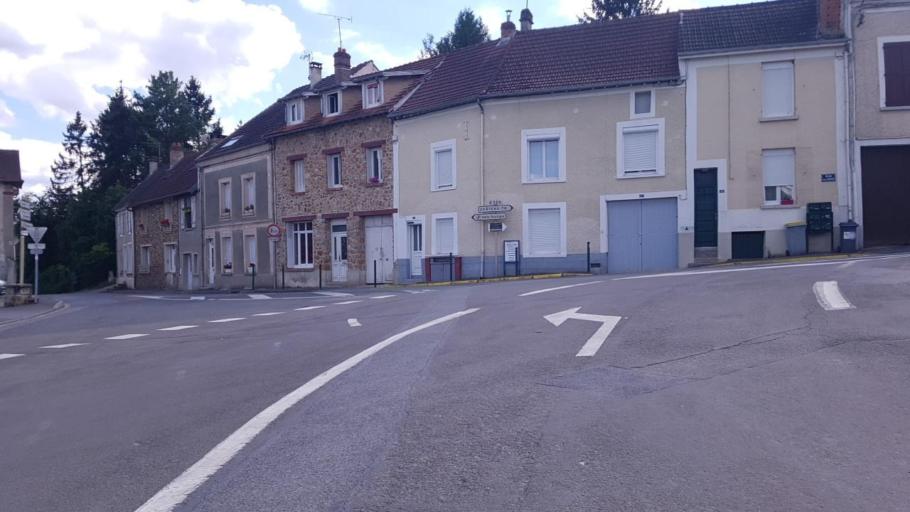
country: FR
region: Picardie
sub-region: Departement de l'Aisne
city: Crezancy
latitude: 49.0883
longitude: 3.5356
